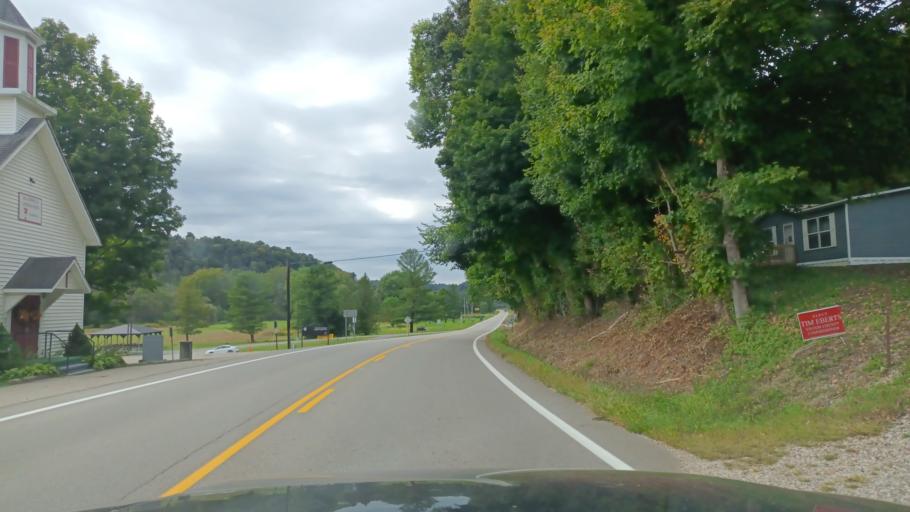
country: US
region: Ohio
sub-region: Vinton County
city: McArthur
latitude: 39.2728
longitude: -82.6085
